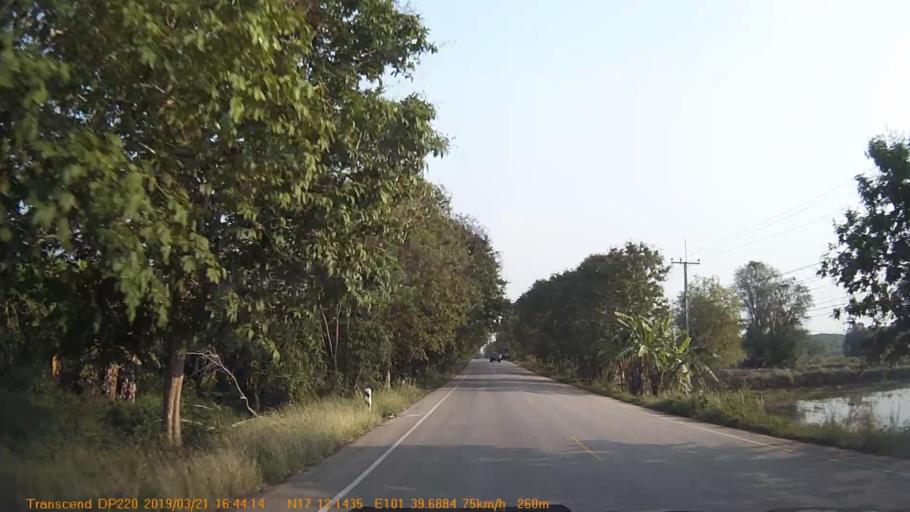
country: TH
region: Loei
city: Phu Luang
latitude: 17.2022
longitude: 101.6615
